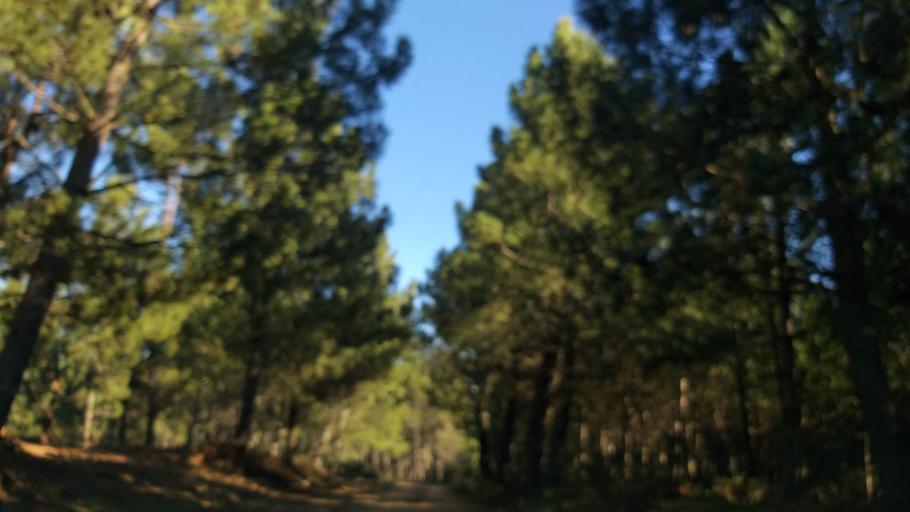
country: PT
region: Guarda
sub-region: Celorico da Beira
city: Celorico da Beira
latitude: 40.5147
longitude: -7.4079
